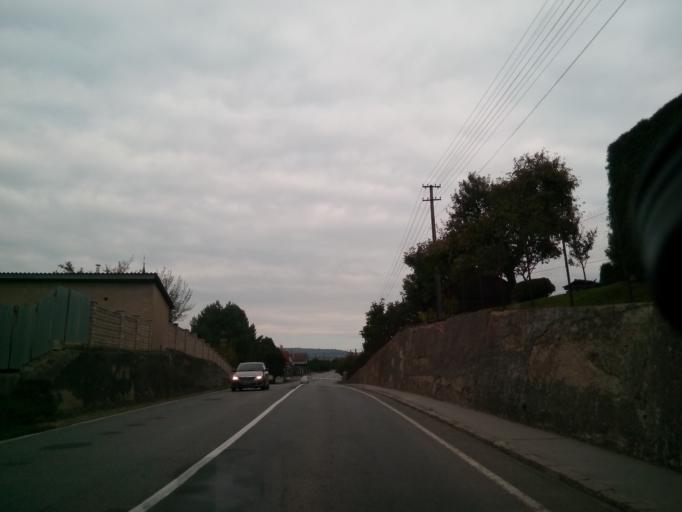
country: SK
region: Presovsky
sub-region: Okres Presov
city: Presov
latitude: 49.0878
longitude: 21.3136
